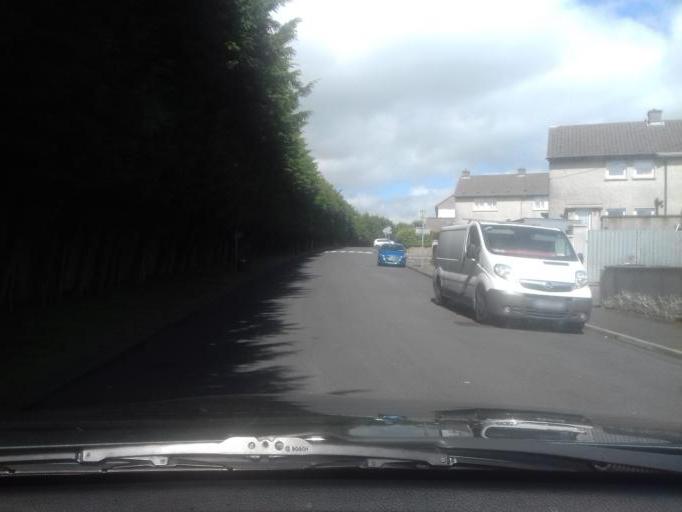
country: IE
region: Leinster
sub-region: Laois
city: Portlaoise
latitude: 53.0407
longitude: -7.2949
